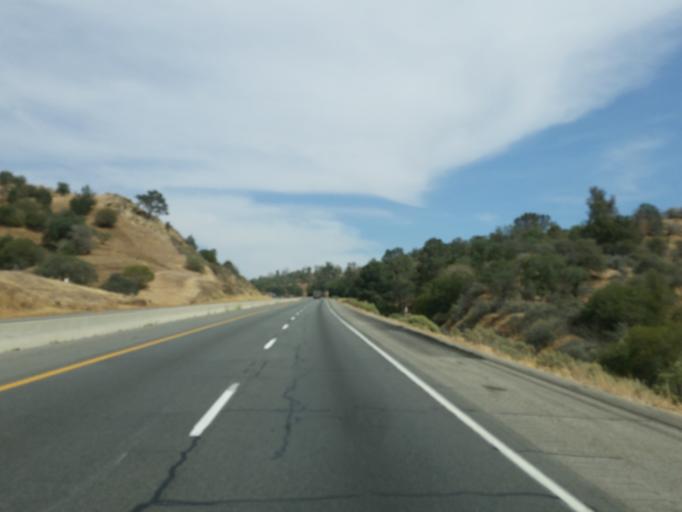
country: US
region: California
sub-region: Kern County
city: Bear Valley Springs
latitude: 35.2539
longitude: -118.6069
